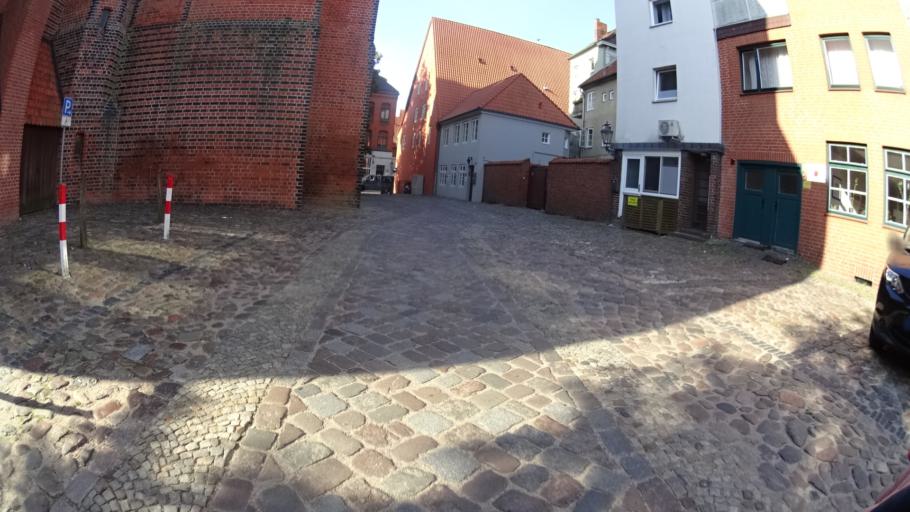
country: DE
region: Lower Saxony
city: Lueneburg
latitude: 53.2519
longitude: 10.4097
